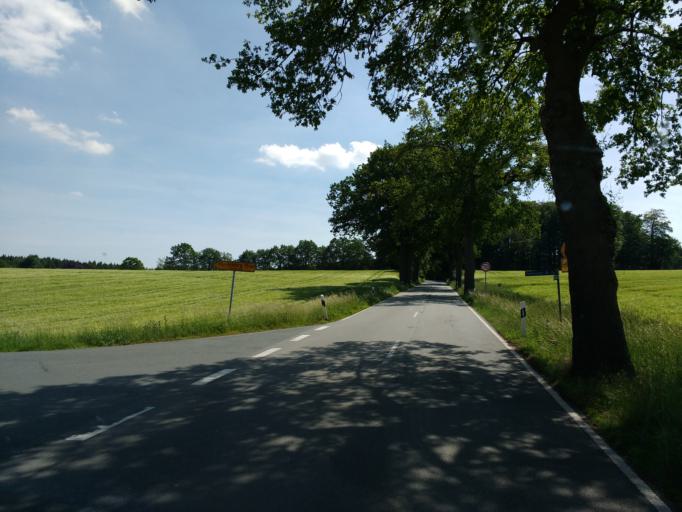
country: DE
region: Lower Saxony
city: Belm
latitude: 52.3671
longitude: 8.1059
